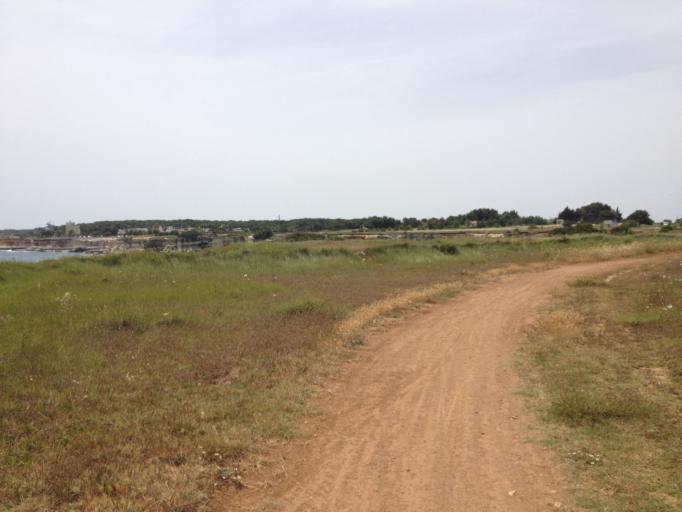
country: IT
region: Apulia
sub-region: Provincia di Lecce
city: Borgagne
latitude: 40.2608
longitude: 18.4434
